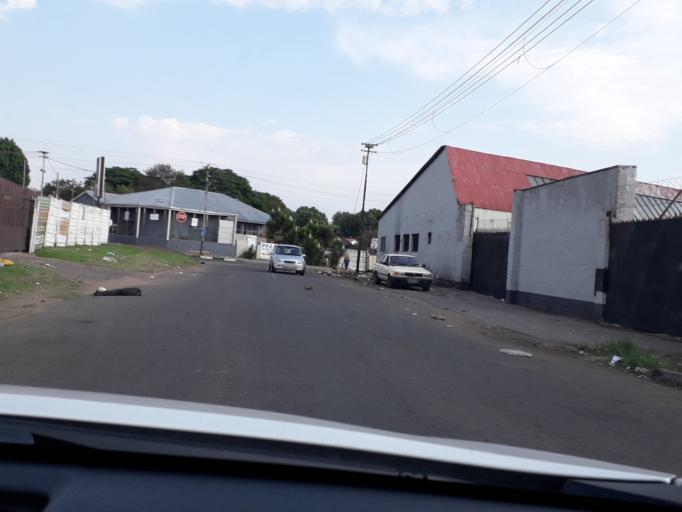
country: ZA
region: Gauteng
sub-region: City of Johannesburg Metropolitan Municipality
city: Johannesburg
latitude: -26.1795
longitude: 27.9663
